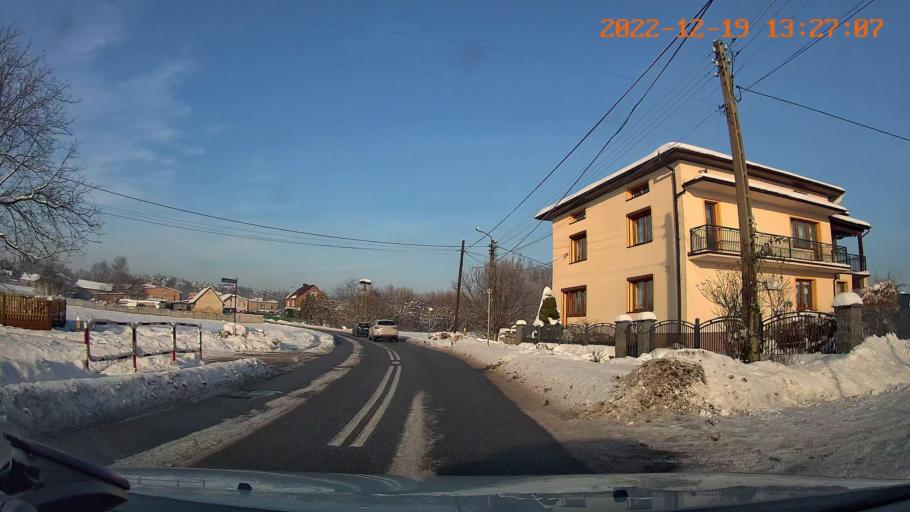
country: PL
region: Silesian Voivodeship
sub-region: Powiat bierunsko-ledzinski
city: Ledziny
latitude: 50.1054
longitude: 19.1370
